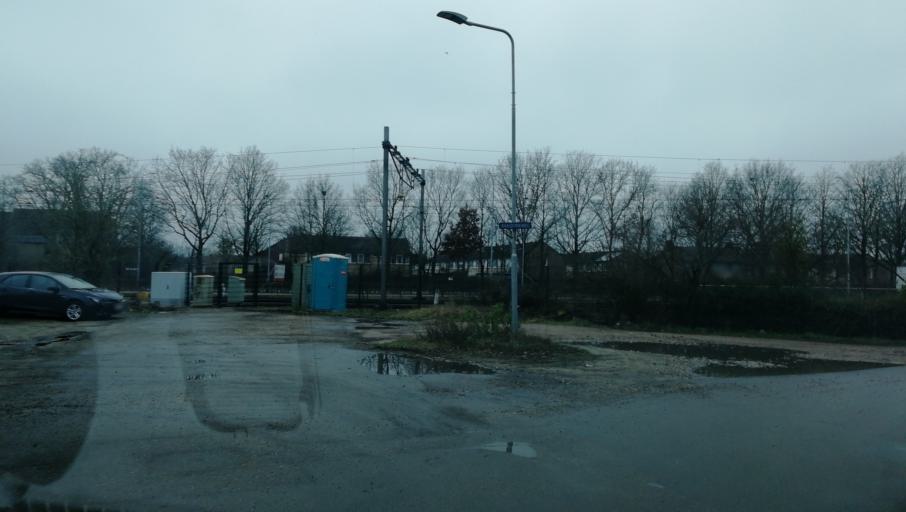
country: NL
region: Limburg
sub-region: Gemeente Venlo
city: Venlo
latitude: 51.3784
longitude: 6.1443
